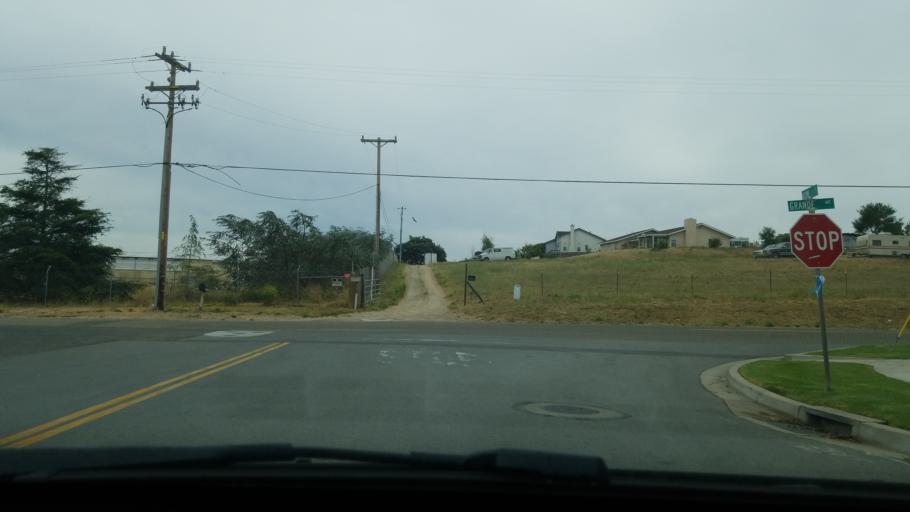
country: US
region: California
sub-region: San Luis Obispo County
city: Nipomo
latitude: 35.0301
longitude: -120.4857
